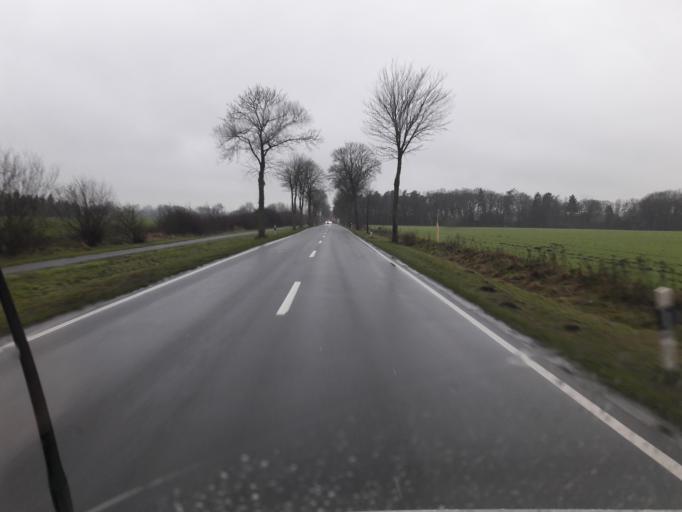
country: DE
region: Lower Saxony
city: Warmsen
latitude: 52.4792
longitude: 8.8774
